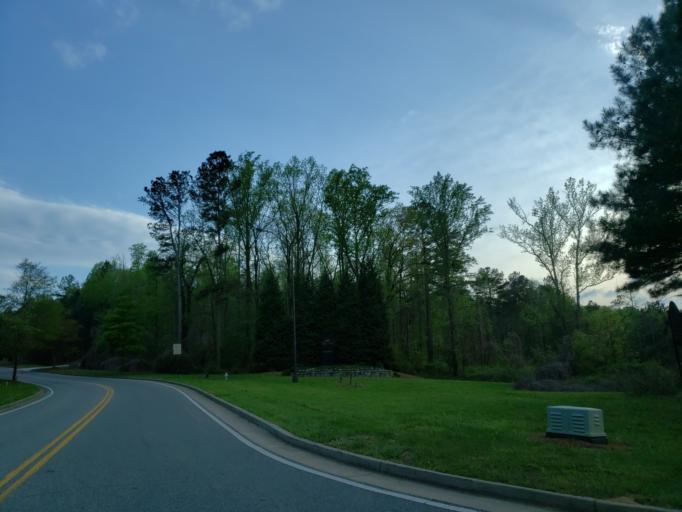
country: US
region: Georgia
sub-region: Cherokee County
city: Canton
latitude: 34.2924
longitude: -84.4632
